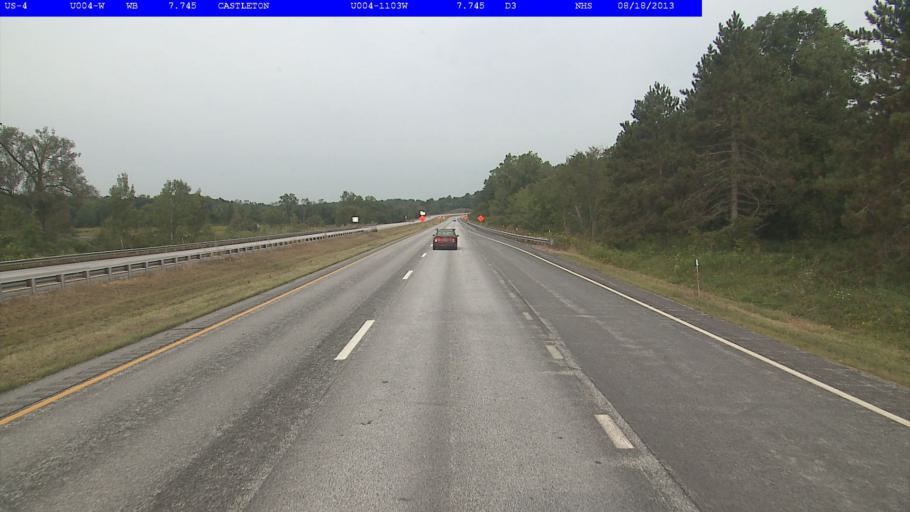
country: US
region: Vermont
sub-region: Rutland County
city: Castleton
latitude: 43.6168
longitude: -73.1659
